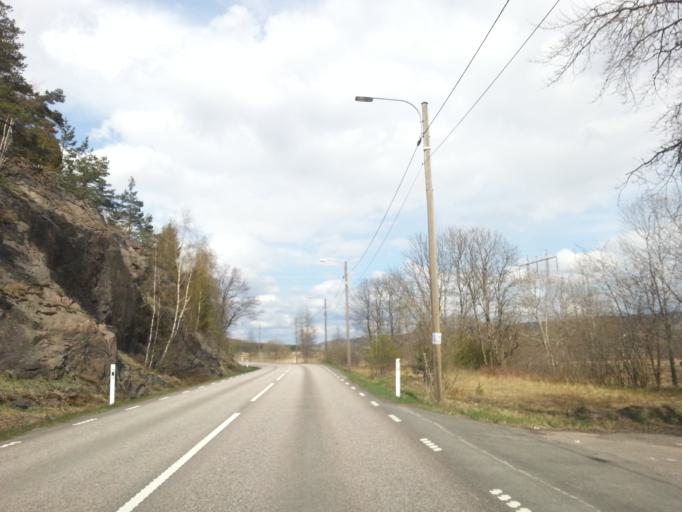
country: SE
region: Vaestra Goetaland
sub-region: Ale Kommun
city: Surte
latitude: 57.8147
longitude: 12.0004
